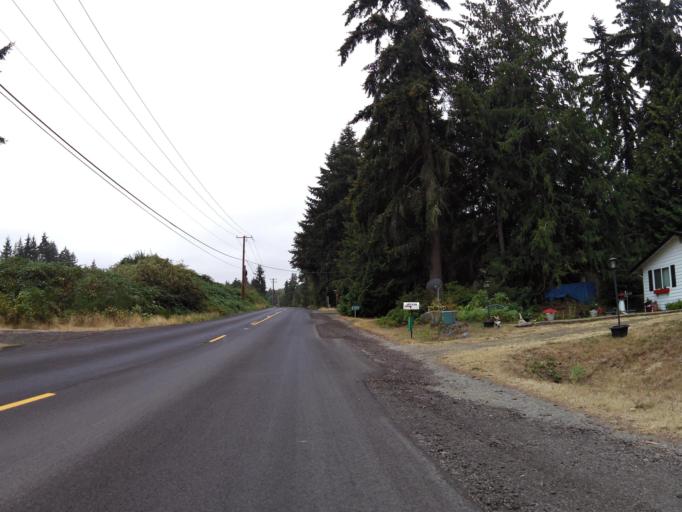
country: US
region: Washington
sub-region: Kitsap County
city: Lofall
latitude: 47.8035
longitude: -122.6600
